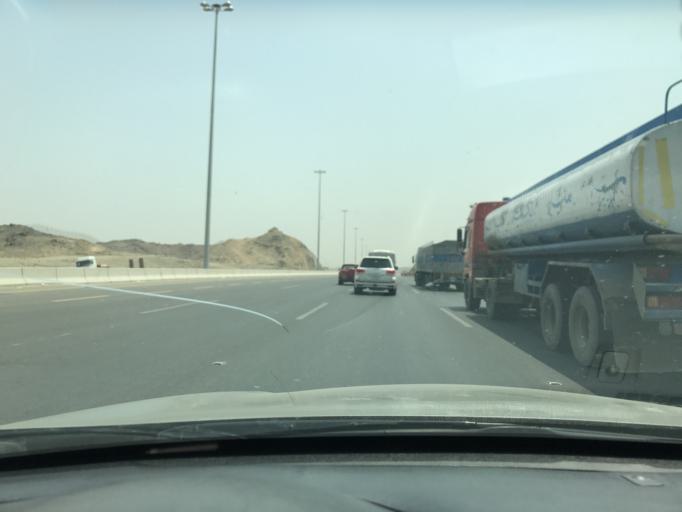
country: SA
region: Makkah
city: Jeddah
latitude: 21.6154
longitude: 39.2561
